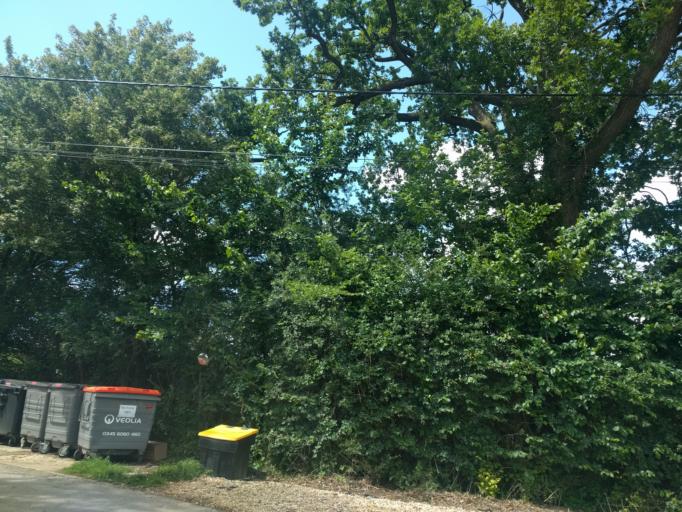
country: GB
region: England
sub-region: West Berkshire
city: Kintbury
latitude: 51.3855
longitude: -1.4071
